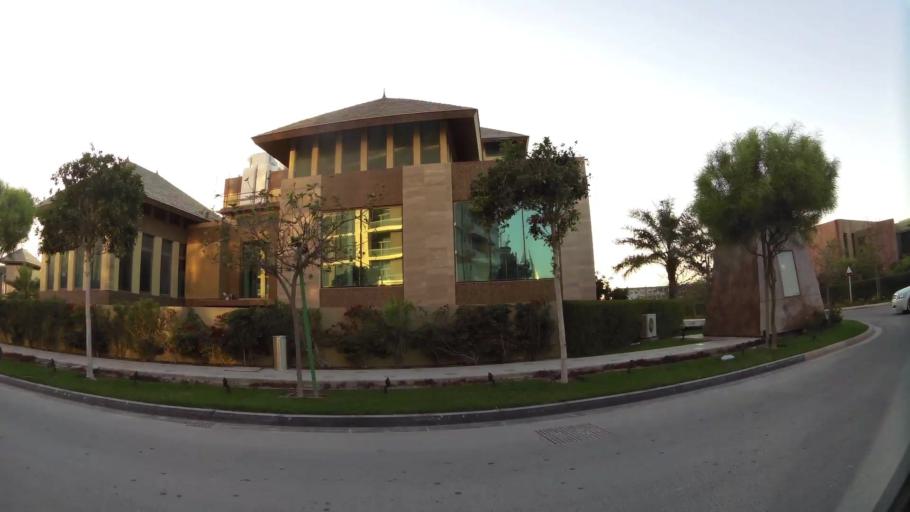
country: BH
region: Manama
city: Jidd Hafs
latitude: 26.2435
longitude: 50.5673
